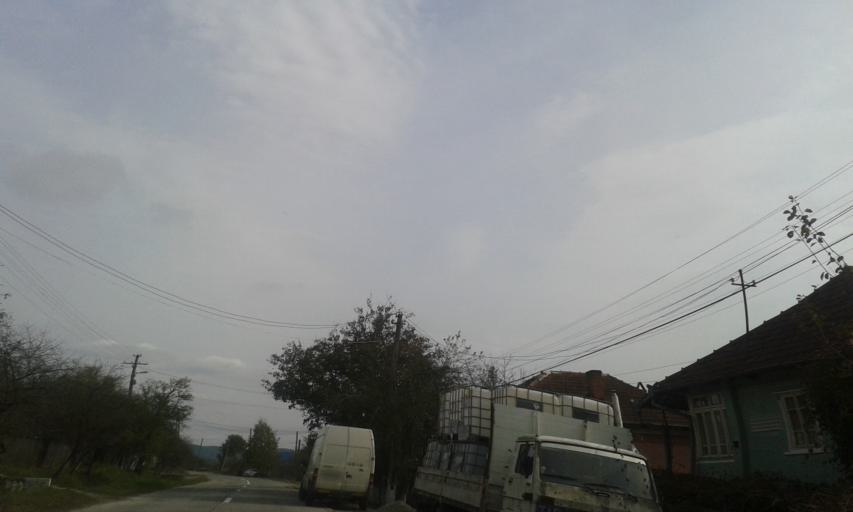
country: RO
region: Valcea
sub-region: Comuna Gradistea
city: Gradistea
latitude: 44.9009
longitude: 23.8080
